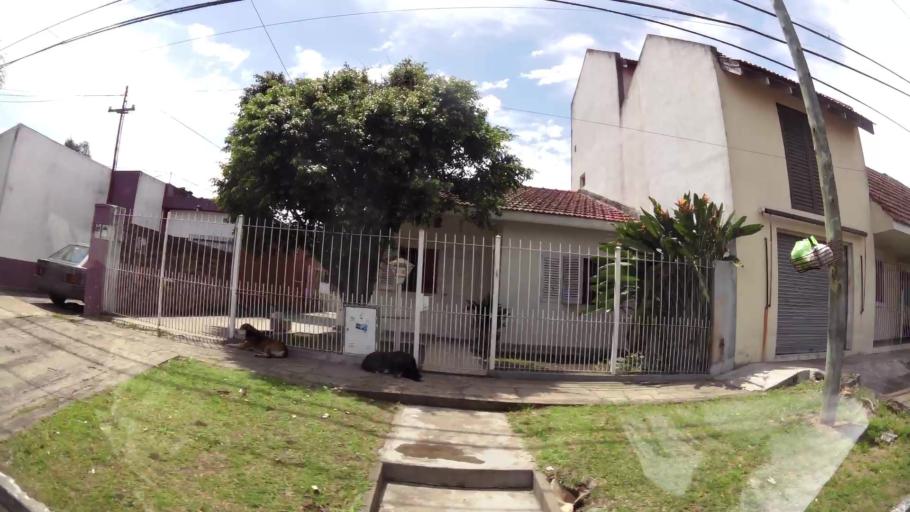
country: AR
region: Buenos Aires
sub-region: Partido de Quilmes
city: Quilmes
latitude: -34.7777
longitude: -58.2602
